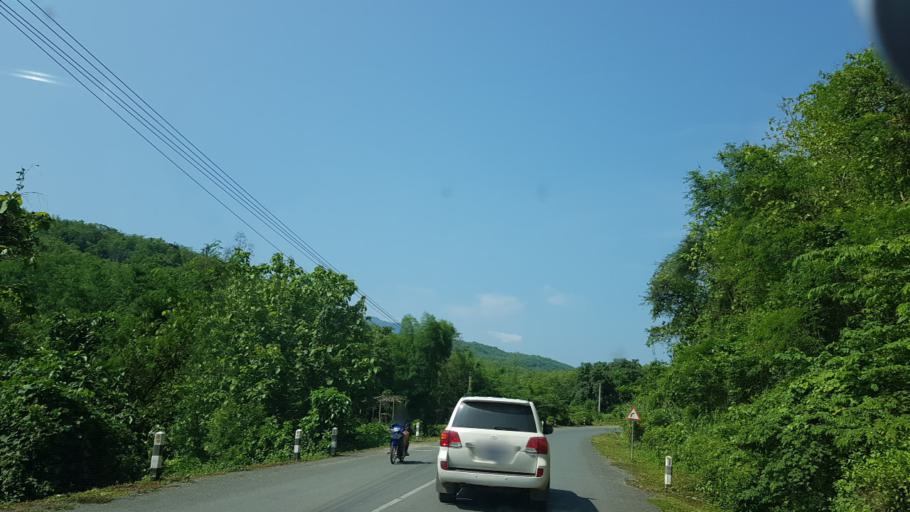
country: LA
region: Louangphabang
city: Xiang Ngeun
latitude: 19.7256
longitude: 102.1521
